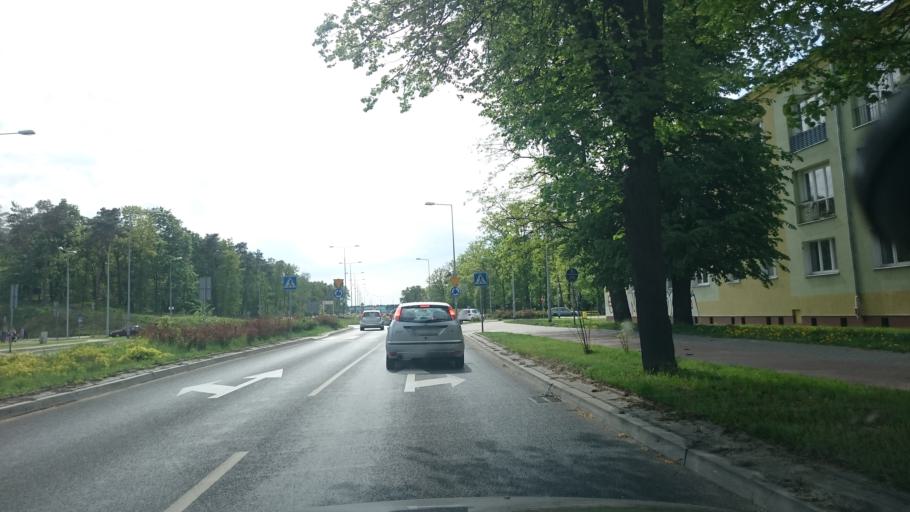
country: PL
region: Kujawsko-Pomorskie
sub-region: Grudziadz
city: Grudziadz
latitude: 53.4729
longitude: 18.7710
